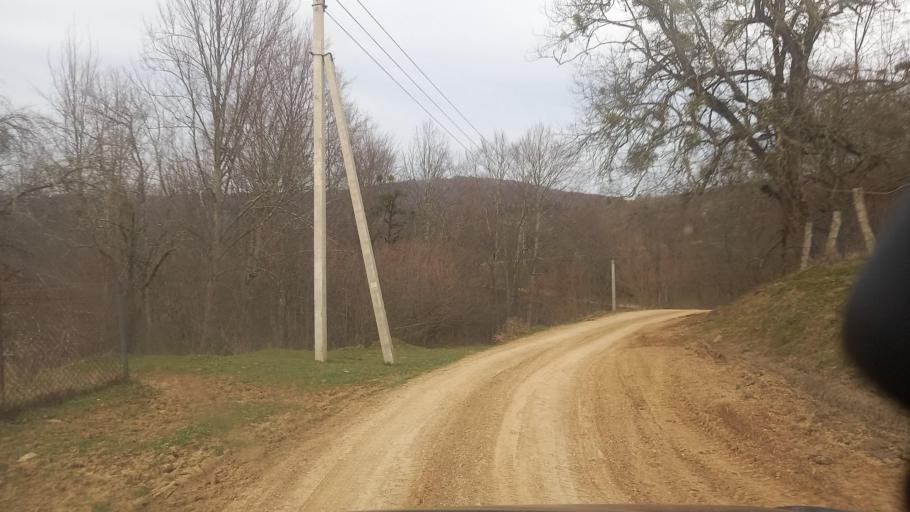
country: RU
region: Adygeya
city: Kamennomostskiy
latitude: 44.2054
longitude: 40.0060
